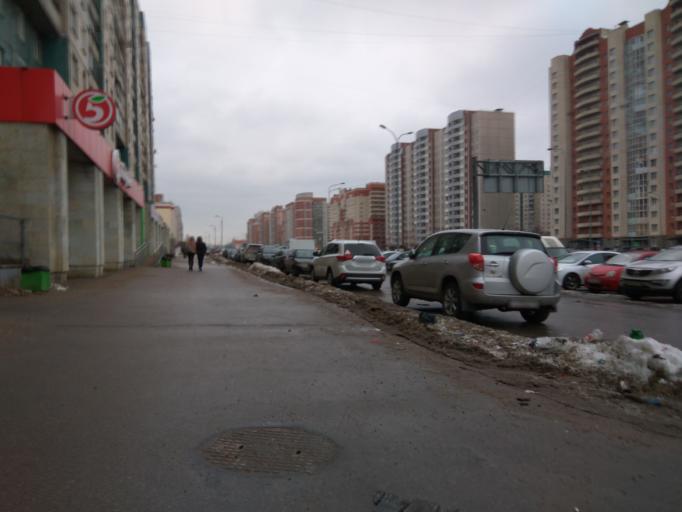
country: RU
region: St.-Petersburg
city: Staraya Derevnya
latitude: 60.0040
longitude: 30.2376
